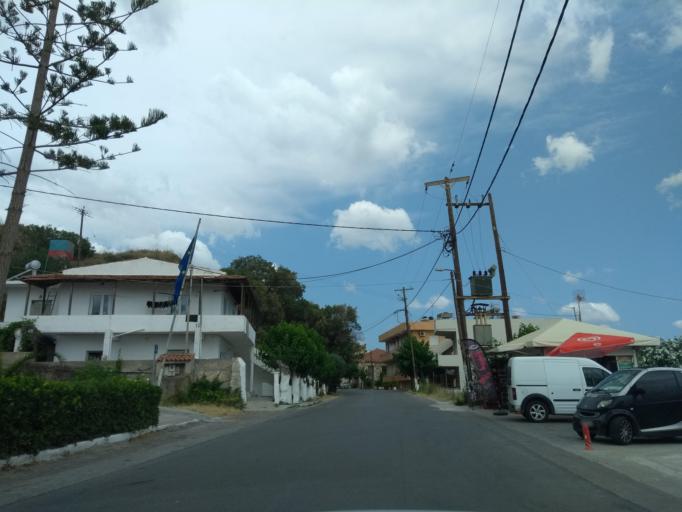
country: GR
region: Crete
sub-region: Nomos Chanias
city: Kalivai
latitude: 35.4571
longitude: 24.1677
